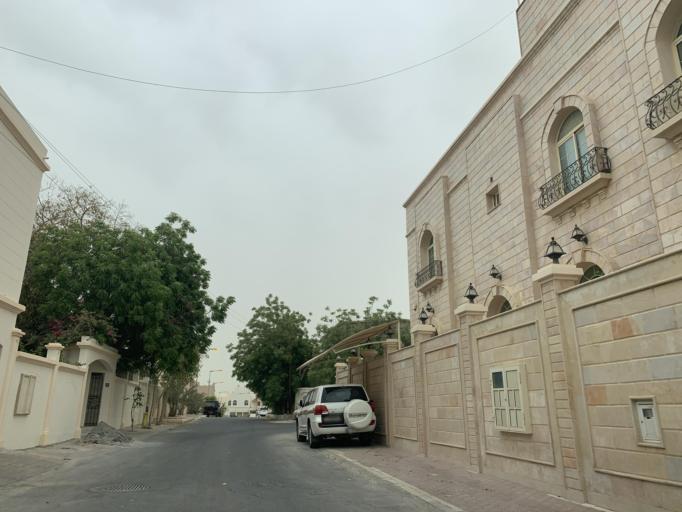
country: BH
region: Central Governorate
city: Madinat Hamad
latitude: 26.1473
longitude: 50.5203
